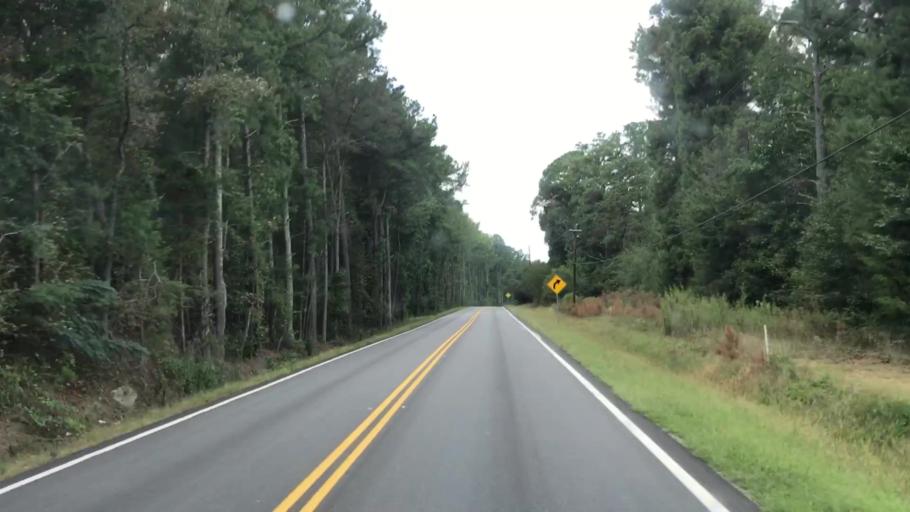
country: US
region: Georgia
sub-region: Greene County
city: Union Point
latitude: 33.5548
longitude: -83.1091
